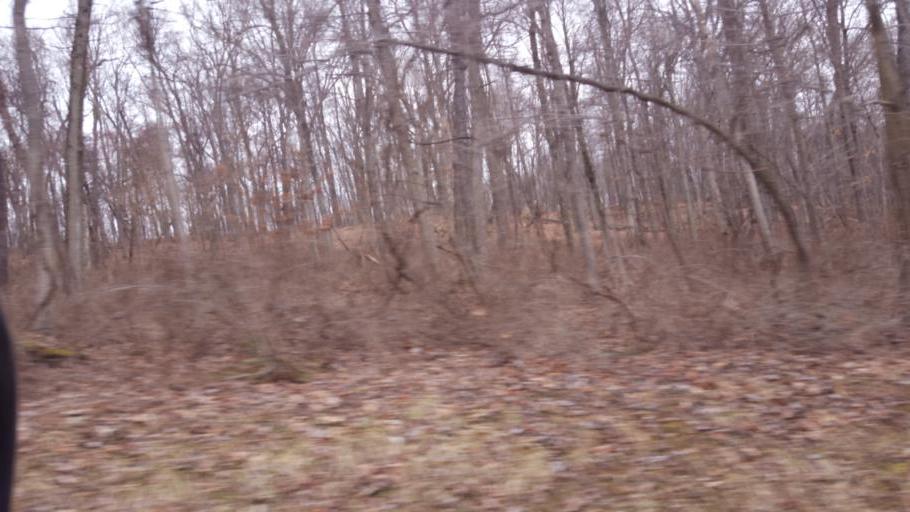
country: US
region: Ohio
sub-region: Ashland County
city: Loudonville
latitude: 40.5694
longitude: -82.2579
